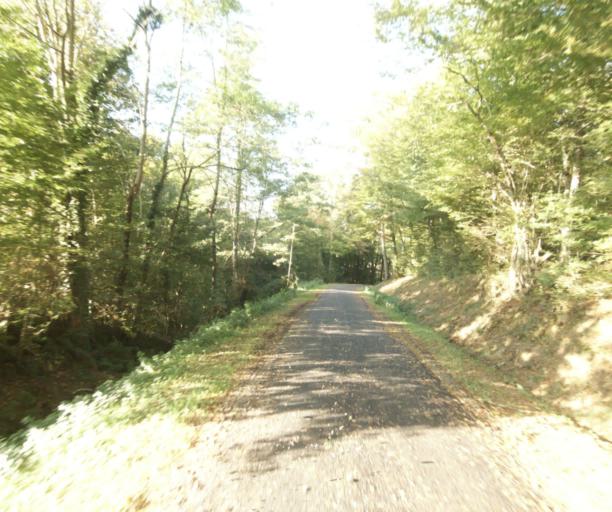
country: FR
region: Midi-Pyrenees
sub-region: Departement du Gers
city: Eauze
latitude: 43.7597
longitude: 0.0915
